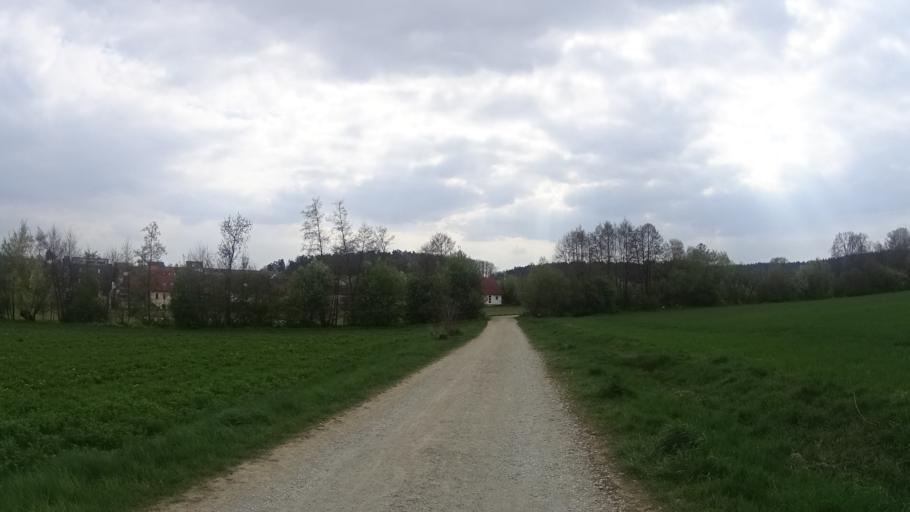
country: DE
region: Bavaria
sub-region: Upper Franconia
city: Igensdorf
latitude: 49.6182
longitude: 11.2195
